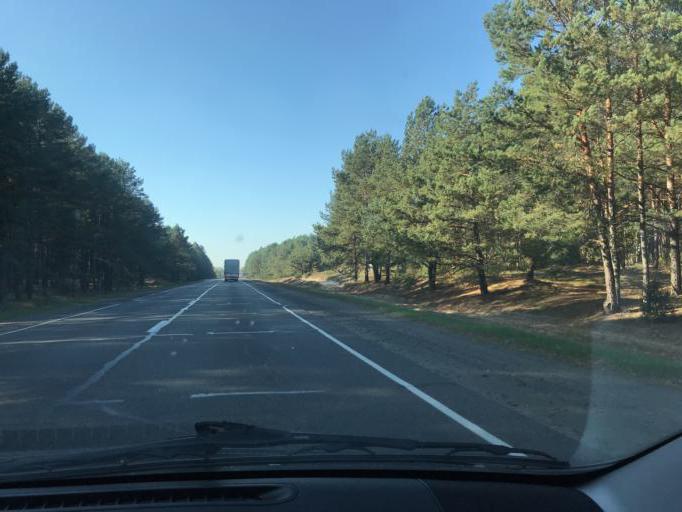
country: BY
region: Brest
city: Davyd-Haradok
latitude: 52.2468
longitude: 27.1037
